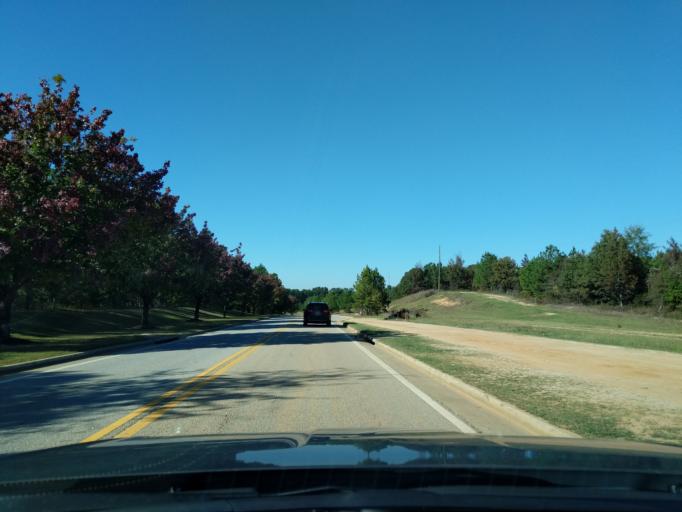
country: US
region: Georgia
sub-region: Columbia County
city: Grovetown
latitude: 33.4630
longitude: -82.1825
